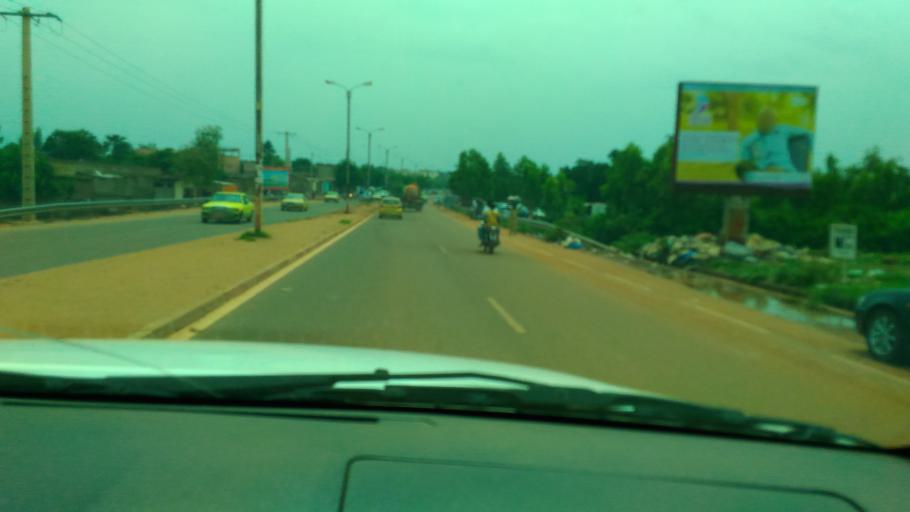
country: ML
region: Bamako
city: Bamako
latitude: 12.5749
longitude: -7.9611
